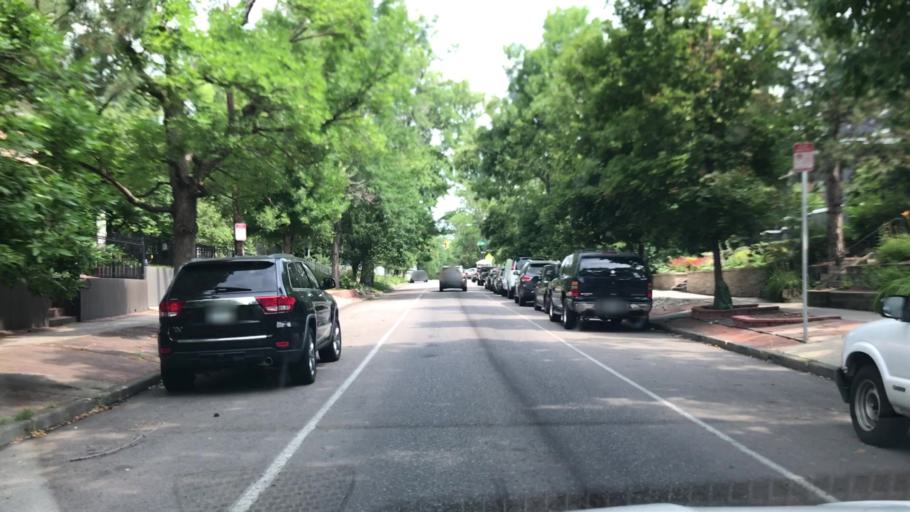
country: US
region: Colorado
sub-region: Denver County
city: Denver
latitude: 39.7280
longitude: -104.9729
